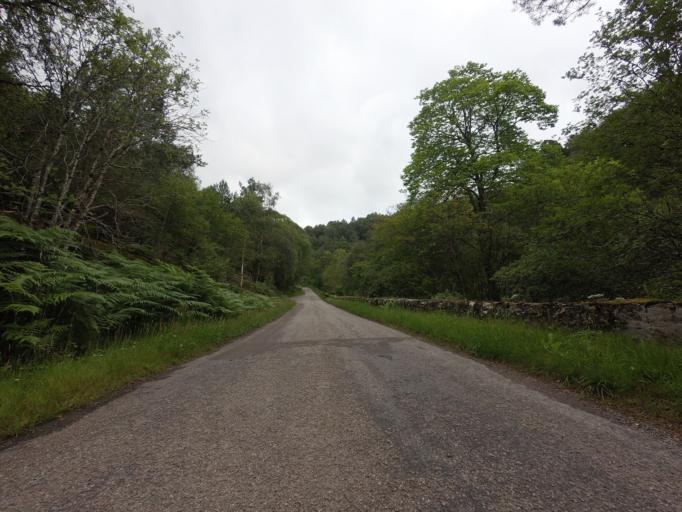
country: GB
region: Scotland
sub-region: Highland
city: Evanton
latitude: 57.9482
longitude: -4.4043
